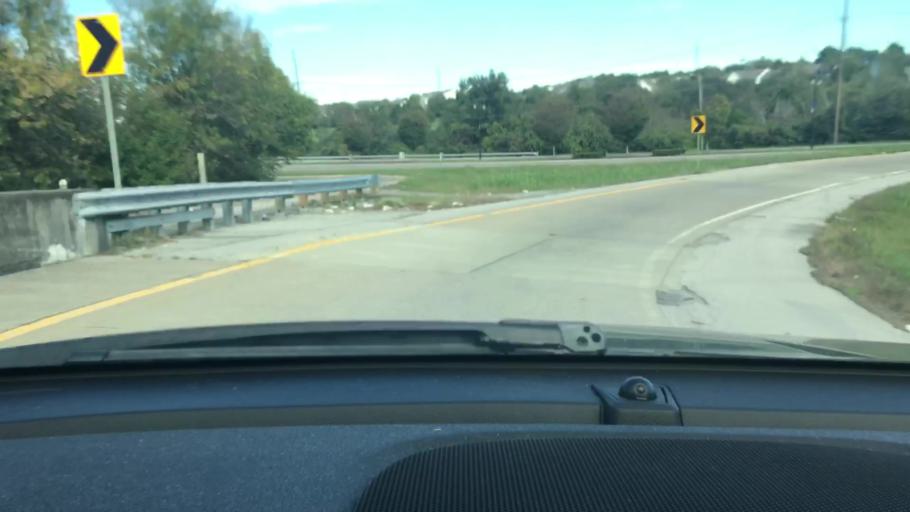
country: US
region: Tennessee
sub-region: Sumner County
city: Hendersonville
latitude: 36.3073
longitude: -86.6587
